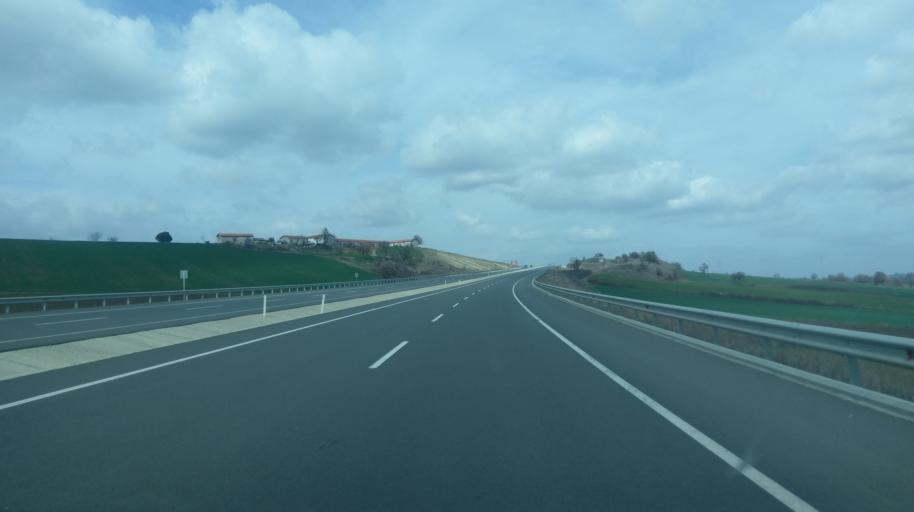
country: TR
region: Edirne
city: Kesan
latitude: 40.9327
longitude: 26.6362
